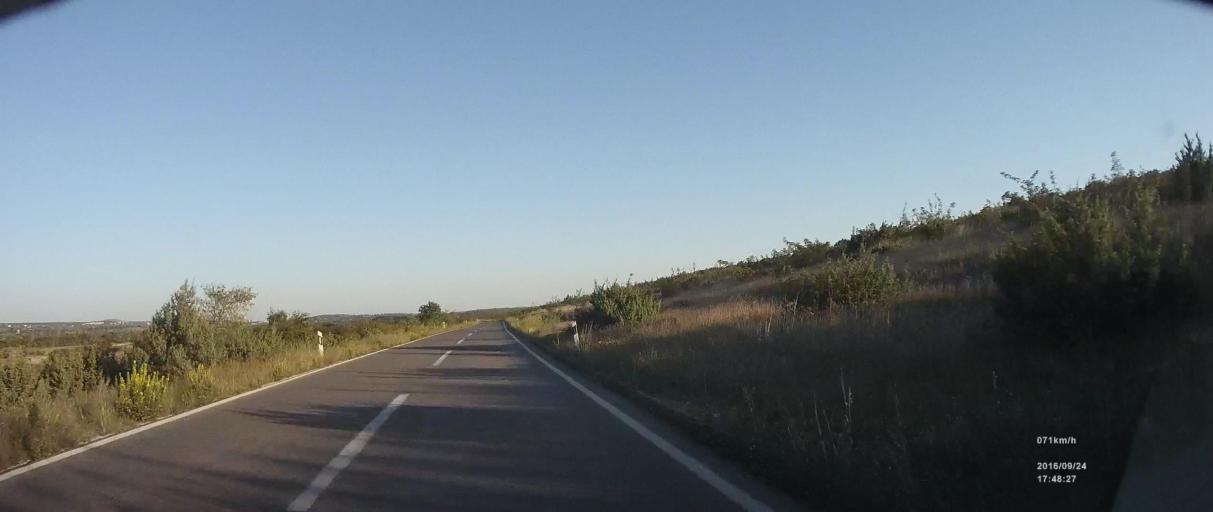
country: HR
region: Zadarska
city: Polaca
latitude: 44.0645
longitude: 15.5367
